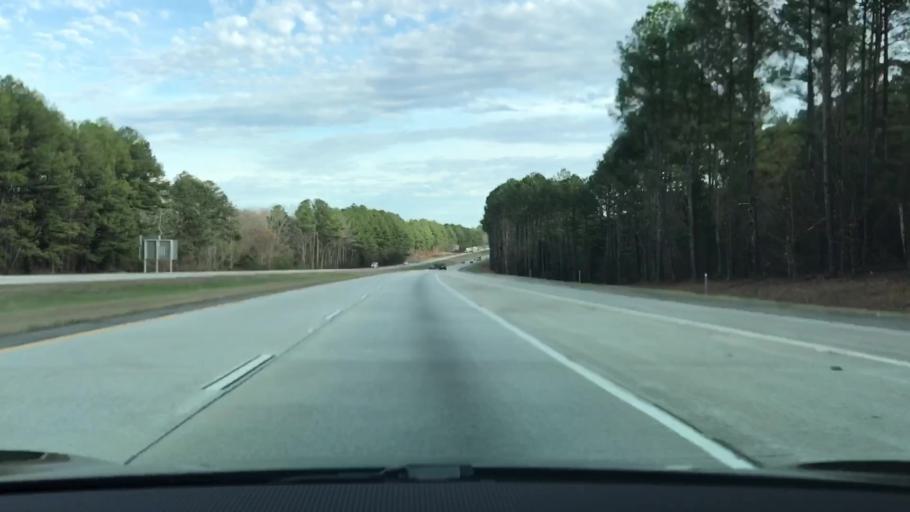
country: US
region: Georgia
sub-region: Taliaferro County
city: Crawfordville
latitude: 33.5295
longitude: -82.9057
